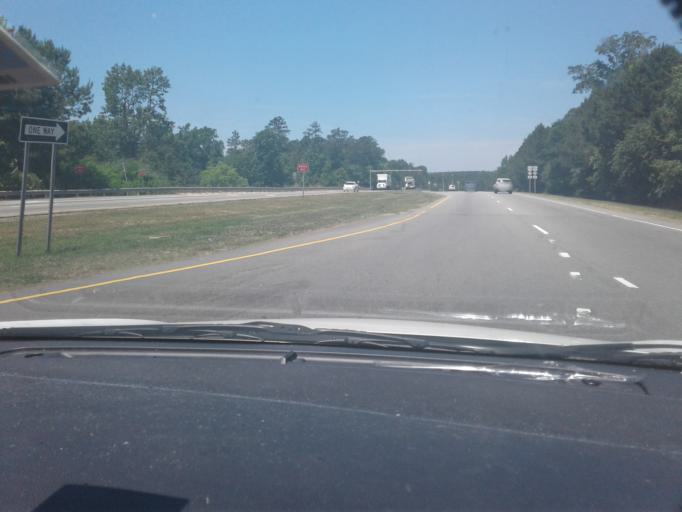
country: US
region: North Carolina
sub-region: Wake County
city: Holly Springs
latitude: 35.6426
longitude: -78.8389
